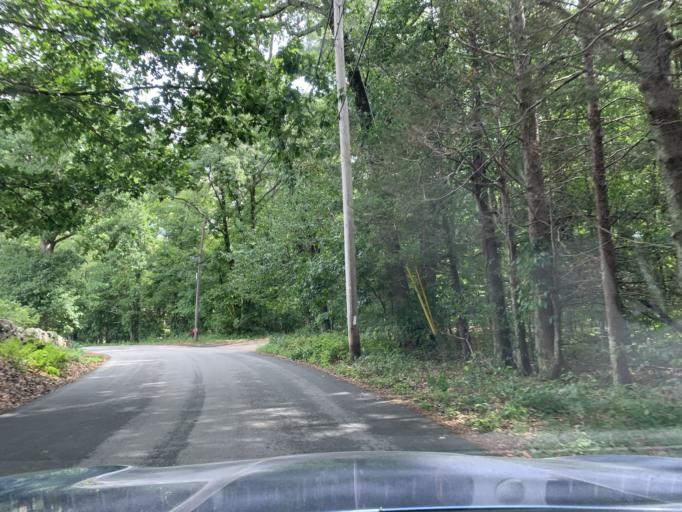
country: US
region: Rhode Island
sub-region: Kent County
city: West Warwick
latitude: 41.7381
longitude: -71.6000
